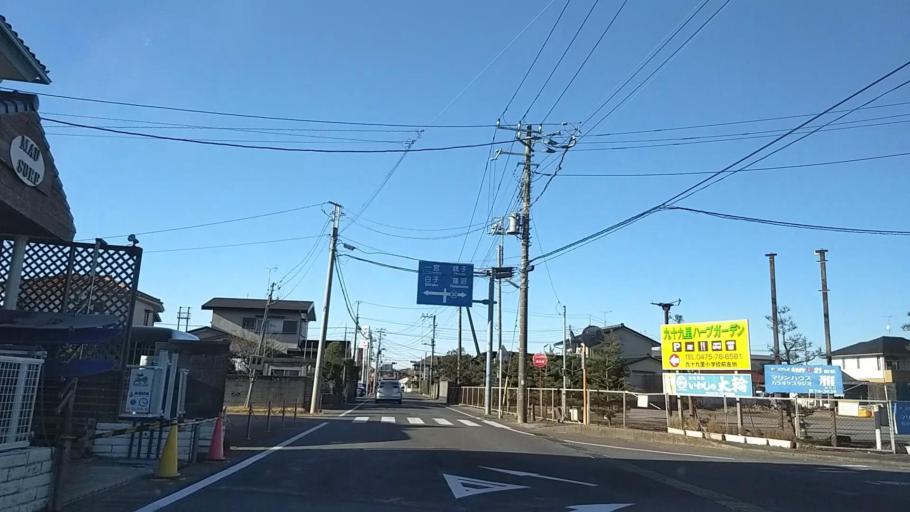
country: JP
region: Chiba
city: Naruto
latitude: 35.5390
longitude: 140.4544
